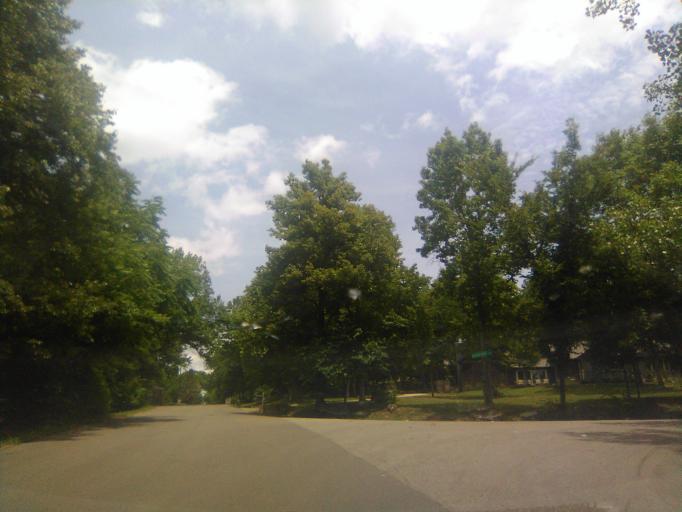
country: US
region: Tennessee
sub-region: Davidson County
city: Belle Meade
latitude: 36.0859
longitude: -86.8500
